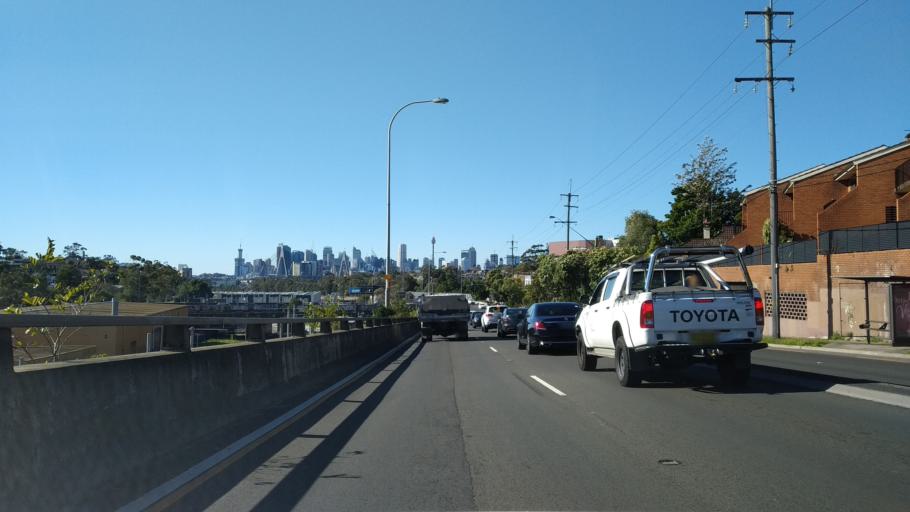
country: AU
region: New South Wales
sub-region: Leichhardt
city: Lilyfield
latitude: -33.8746
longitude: 151.1624
